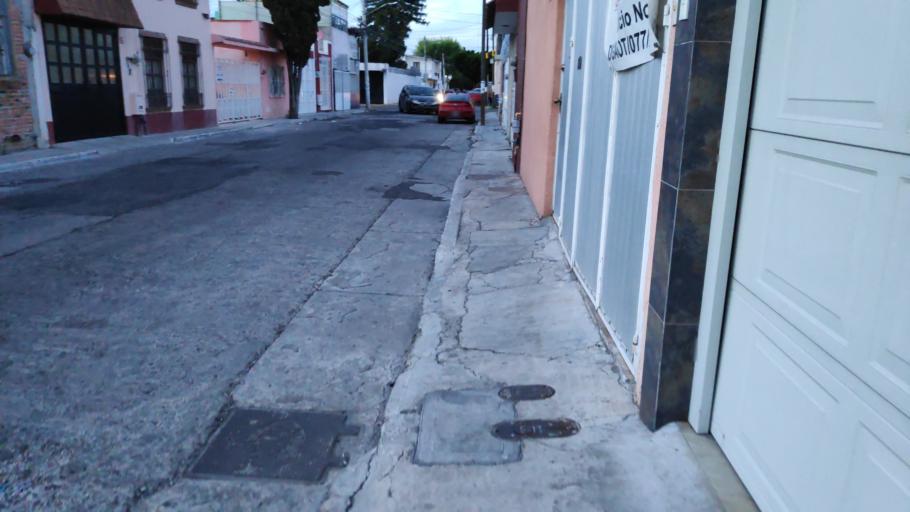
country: MX
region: Queretaro
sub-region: Queretaro
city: Santiago de Queretaro
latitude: 20.5834
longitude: -100.3829
